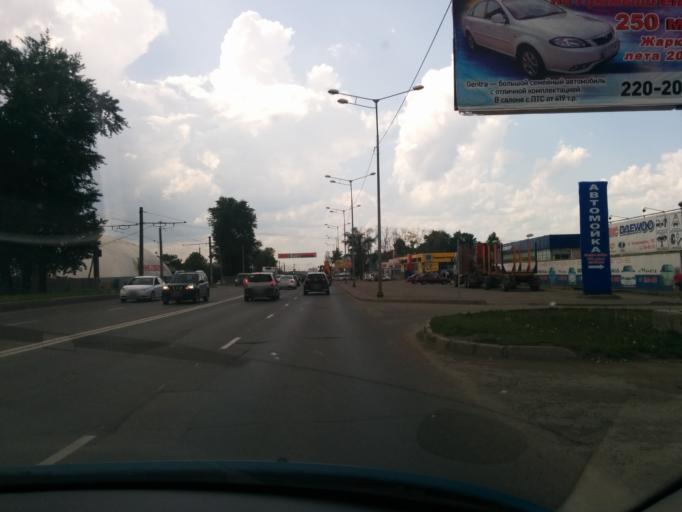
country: RU
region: Perm
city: Kondratovo
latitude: 57.9654
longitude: 56.1428
